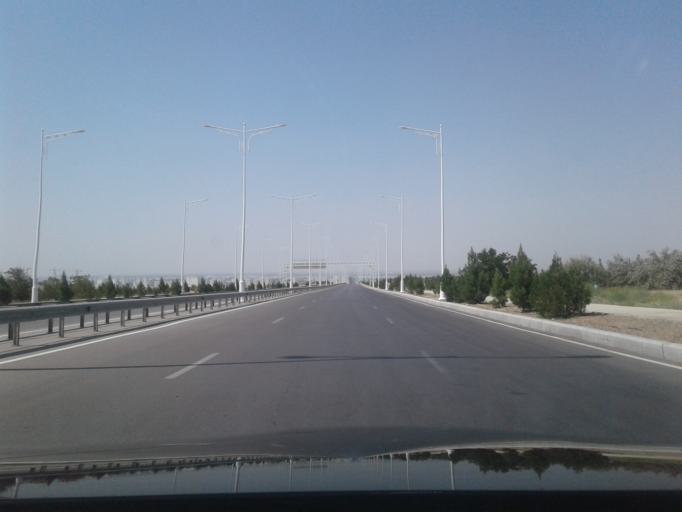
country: TM
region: Ahal
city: Ashgabat
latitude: 37.8798
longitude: 58.4225
